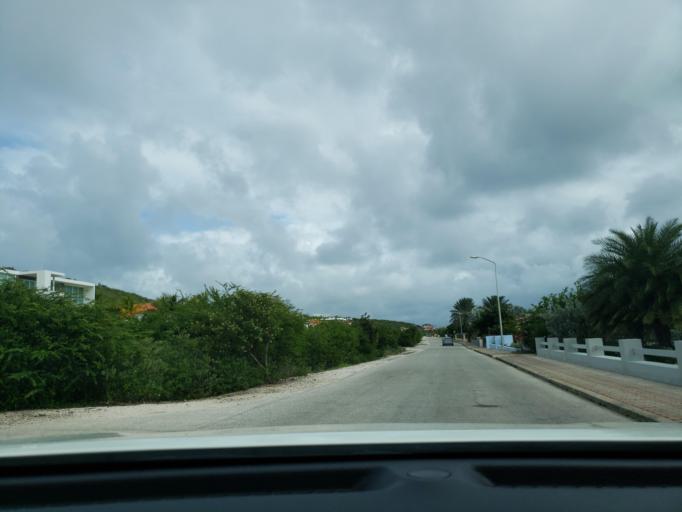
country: CW
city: Dorp Soto
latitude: 12.1965
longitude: -69.0750
